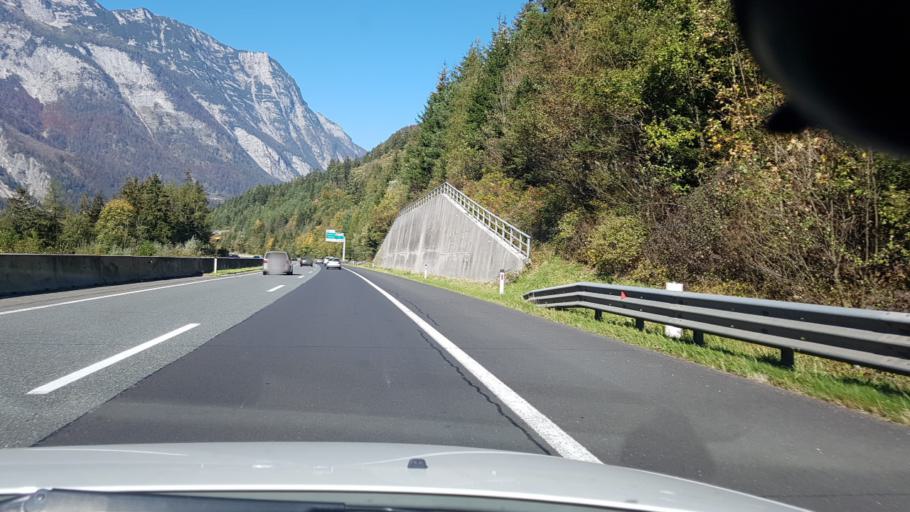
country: AT
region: Salzburg
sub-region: Politischer Bezirk Sankt Johann im Pongau
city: Werfen
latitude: 47.5007
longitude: 13.1795
